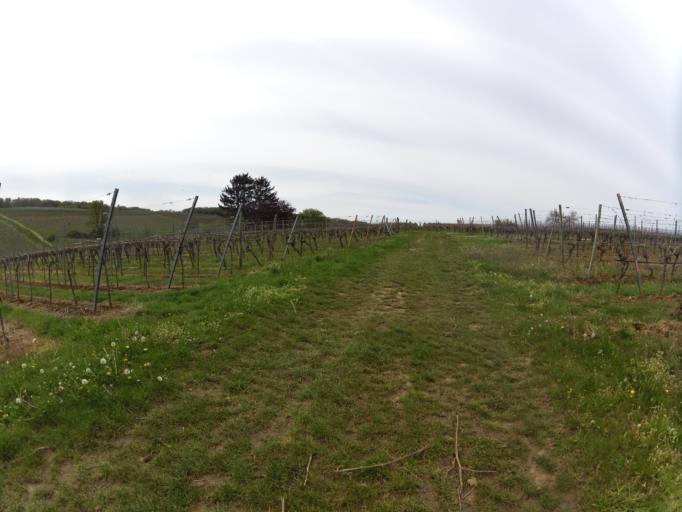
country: DE
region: Bavaria
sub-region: Regierungsbezirk Unterfranken
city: Nordheim
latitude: 49.8628
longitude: 10.1646
